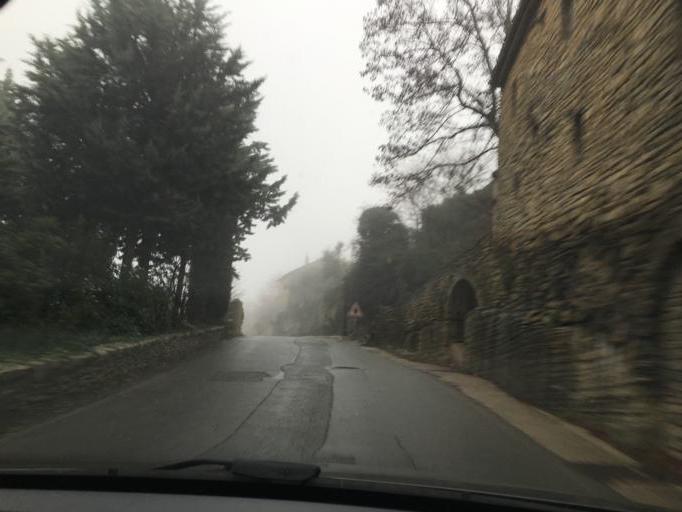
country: FR
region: Provence-Alpes-Cote d'Azur
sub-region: Departement du Vaucluse
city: Gordes
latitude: 43.9136
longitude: 5.1969
